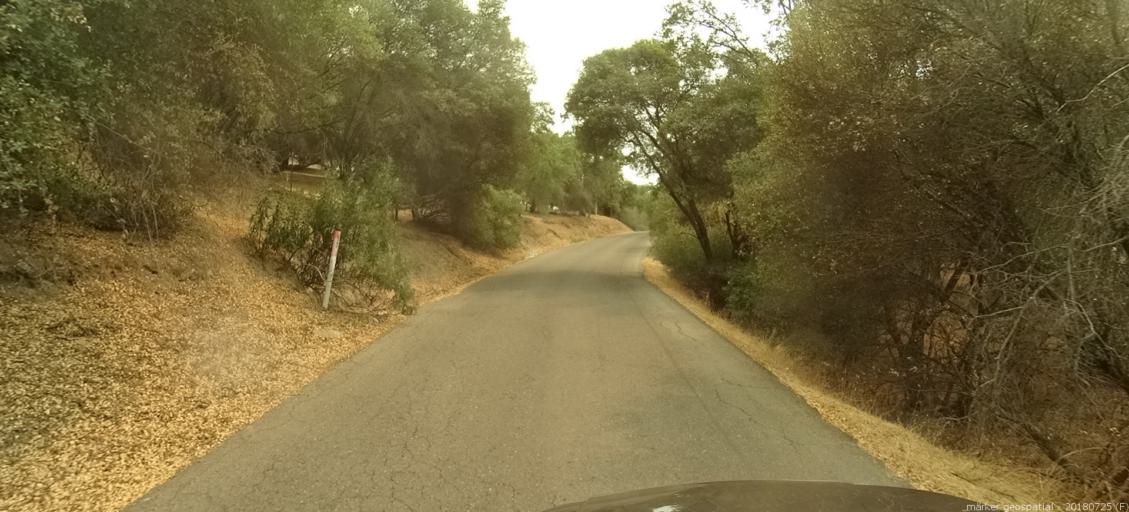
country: US
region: California
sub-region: Madera County
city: Coarsegold
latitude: 37.1936
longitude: -119.6732
